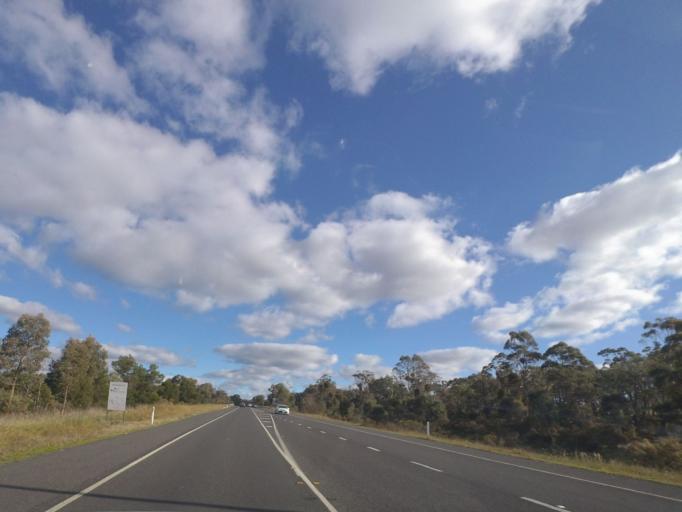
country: AU
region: Victoria
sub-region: Mount Alexander
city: Castlemaine
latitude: -37.0968
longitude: 144.3259
